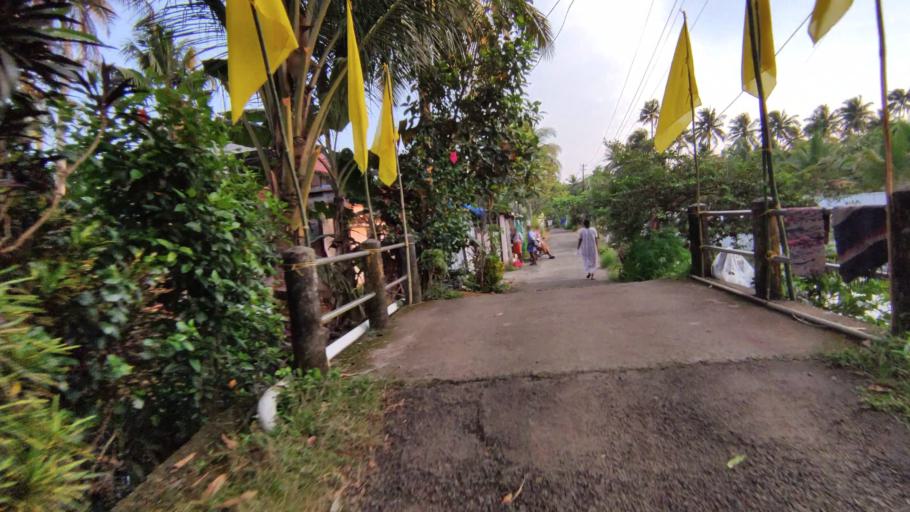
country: IN
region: Kerala
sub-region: Kottayam
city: Kottayam
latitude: 9.5784
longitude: 76.4372
